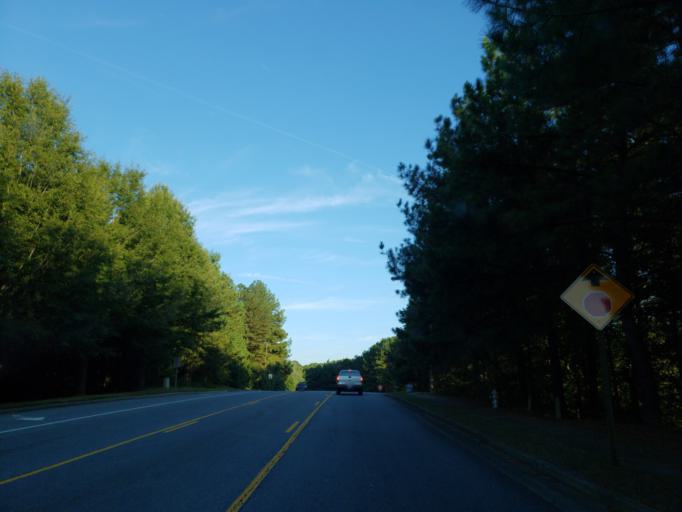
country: US
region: Georgia
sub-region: Cobb County
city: Kennesaw
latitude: 34.0553
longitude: -84.6074
